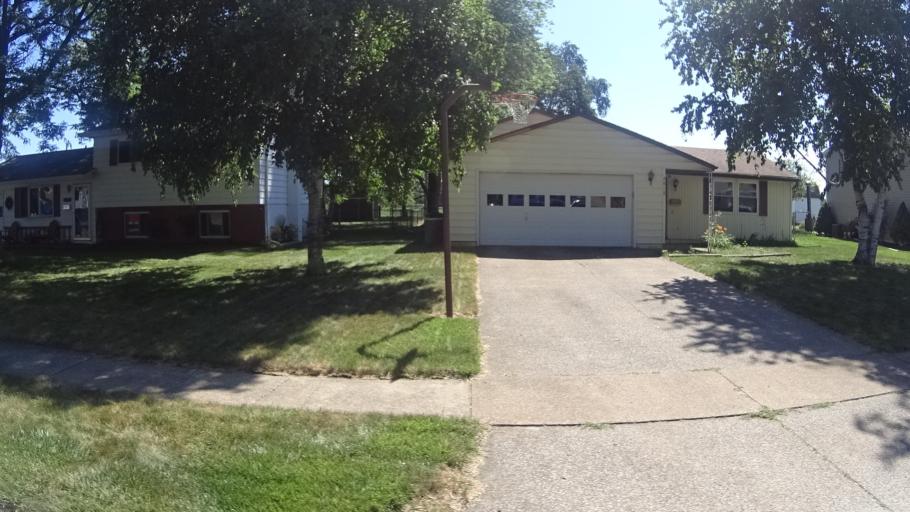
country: US
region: Ohio
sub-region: Erie County
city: Sandusky
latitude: 41.4261
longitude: -82.6518
